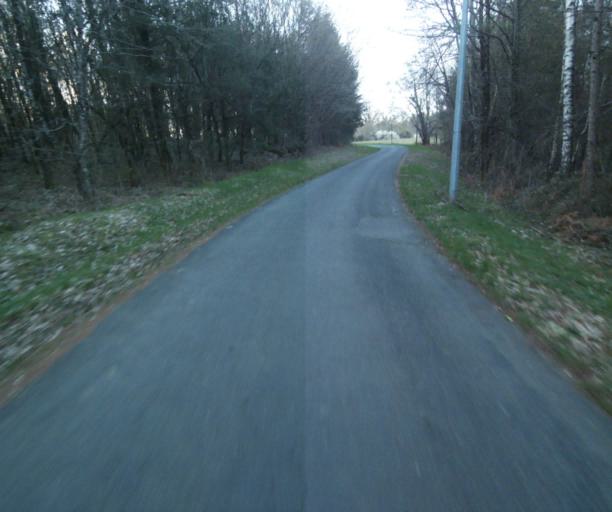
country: FR
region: Limousin
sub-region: Departement de la Correze
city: Uzerche
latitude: 45.3666
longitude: 1.5892
